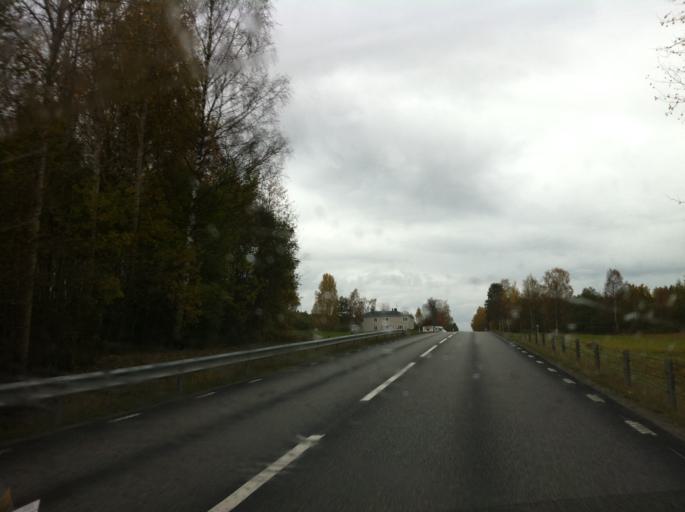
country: SE
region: OErebro
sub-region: Lindesbergs Kommun
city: Stora
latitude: 59.6801
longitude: 15.0990
